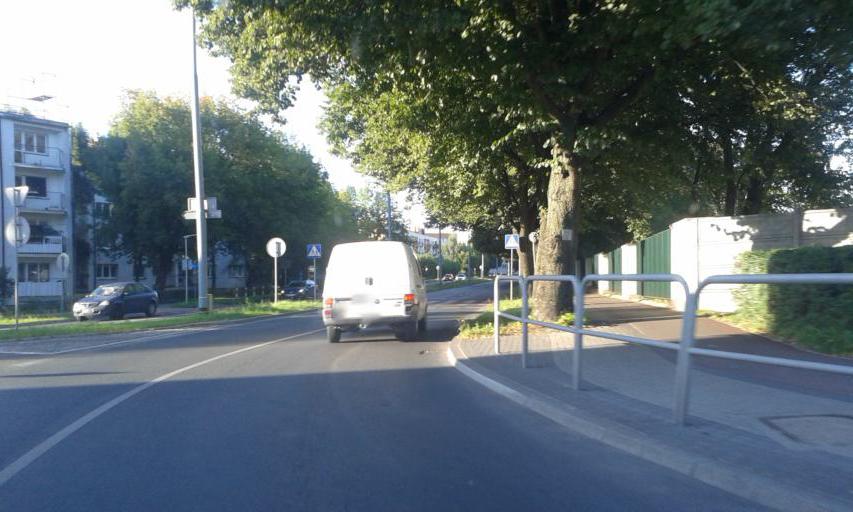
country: PL
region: West Pomeranian Voivodeship
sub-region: Koszalin
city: Koszalin
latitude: 54.1852
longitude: 16.2057
